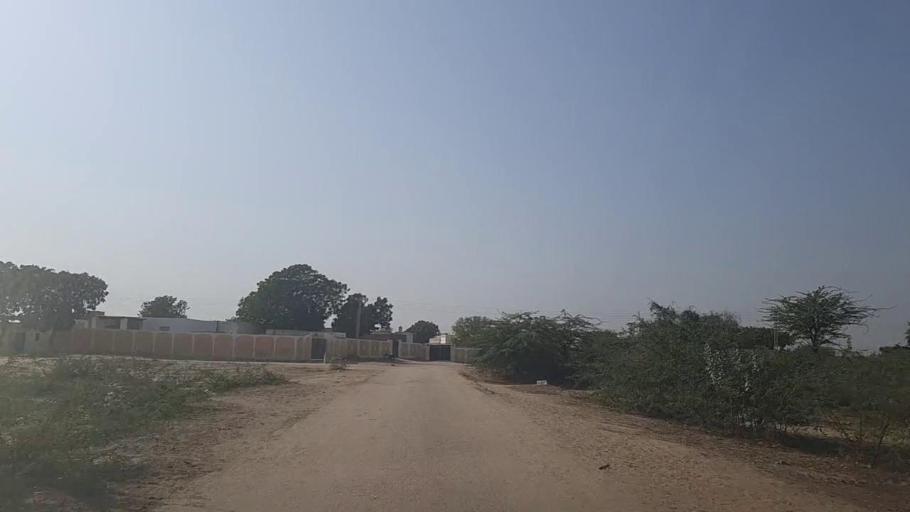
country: PK
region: Sindh
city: Naukot
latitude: 24.8805
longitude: 69.4822
